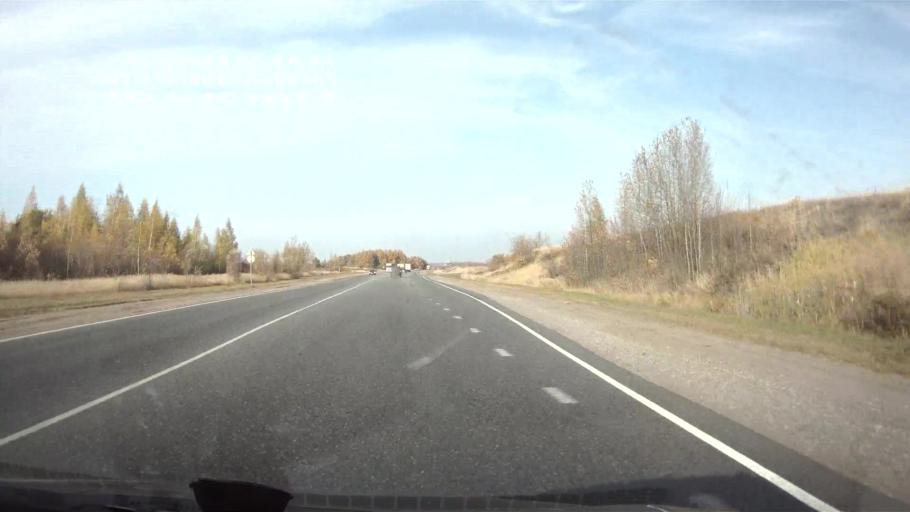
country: RU
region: Chuvashia
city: Kugesi
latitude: 56.0447
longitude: 47.3686
